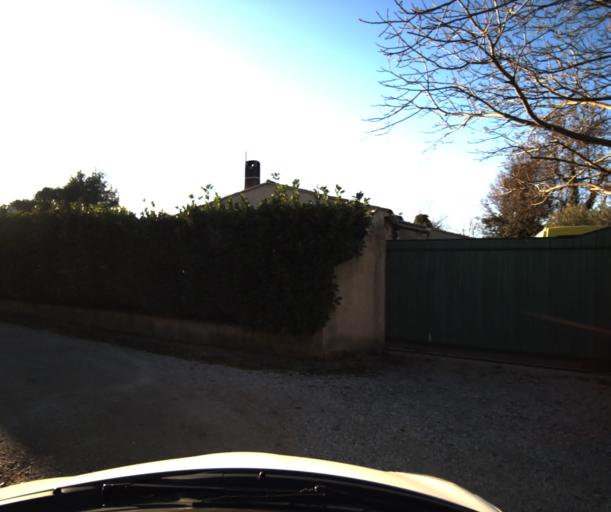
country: FR
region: Provence-Alpes-Cote d'Azur
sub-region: Departement du Vaucluse
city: Pertuis
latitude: 43.6874
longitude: 5.4999
